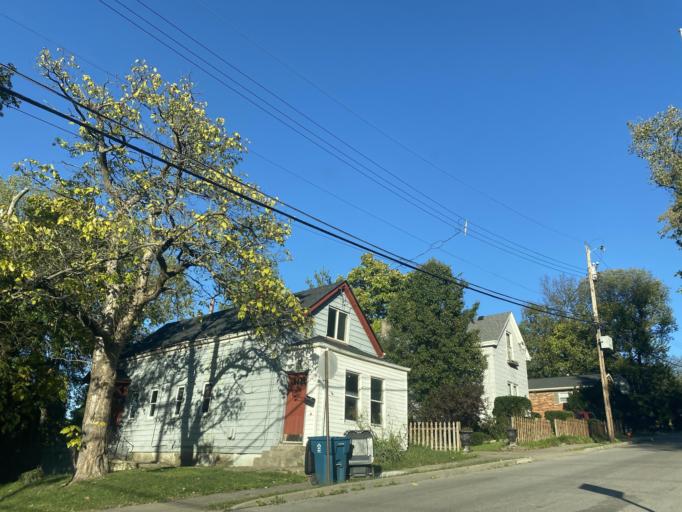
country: US
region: Kentucky
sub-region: Campbell County
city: Dayton
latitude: 39.1128
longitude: -84.4669
